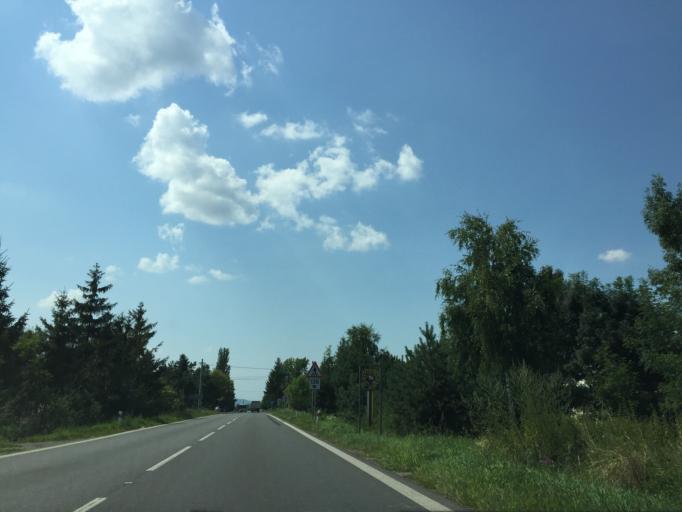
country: SK
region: Kosicky
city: Sobrance
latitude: 48.7538
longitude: 22.1541
